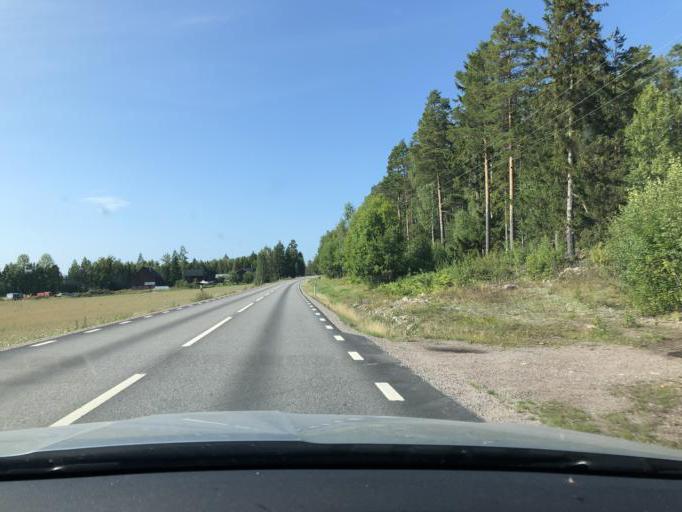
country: SE
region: Dalarna
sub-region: Saters Kommun
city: Saeter
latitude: 60.4083
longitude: 15.8628
